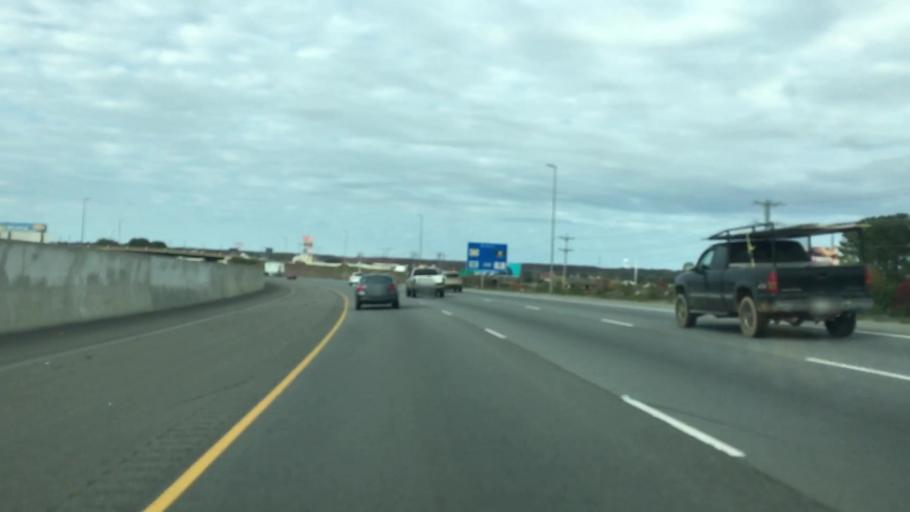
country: US
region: Arkansas
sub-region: Faulkner County
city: Conway
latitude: 35.0809
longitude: -92.4135
